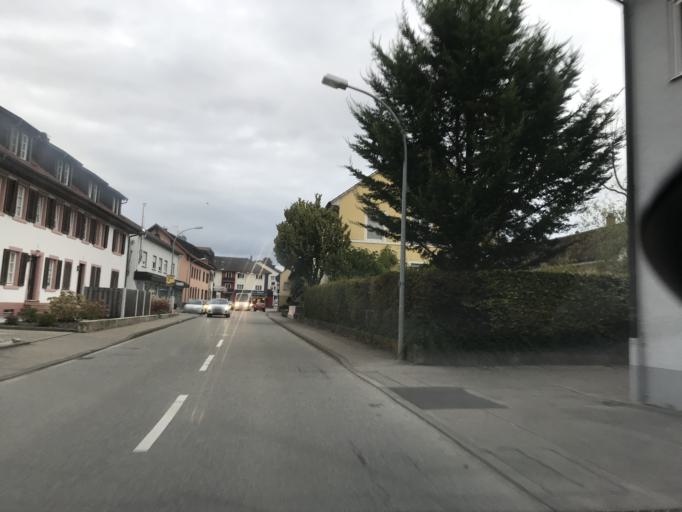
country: DE
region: Baden-Wuerttemberg
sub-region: Freiburg Region
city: Steinen
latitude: 47.6422
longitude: 7.7386
